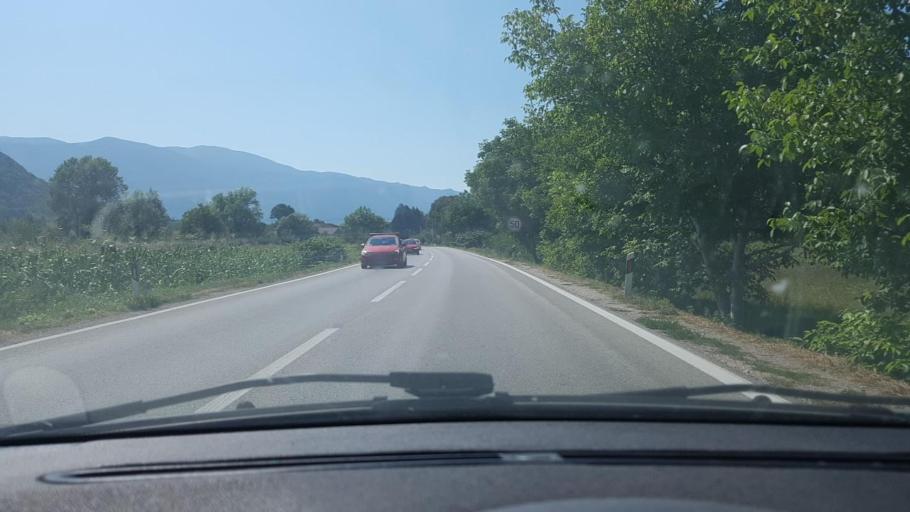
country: BA
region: Federation of Bosnia and Herzegovina
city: Bihac
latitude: 44.8070
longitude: 15.8913
